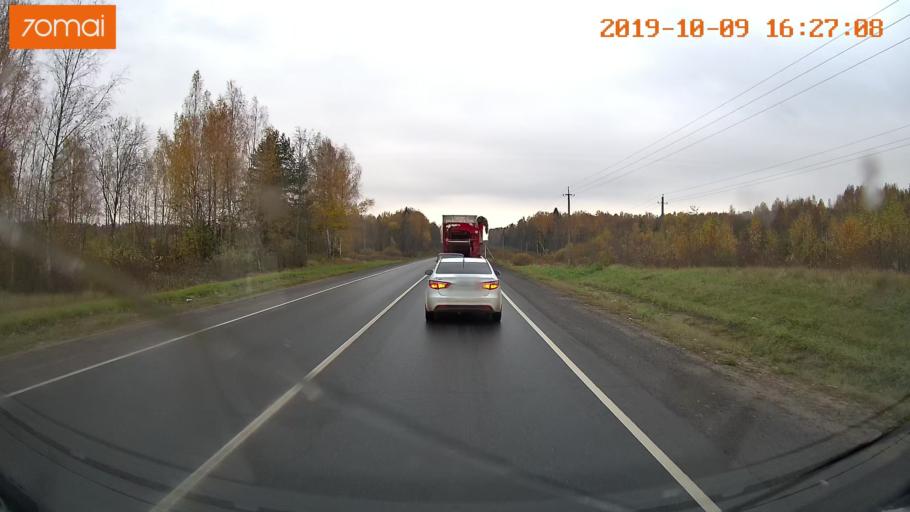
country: RU
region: Kostroma
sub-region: Kostromskoy Rayon
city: Kostroma
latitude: 57.6344
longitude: 40.9270
